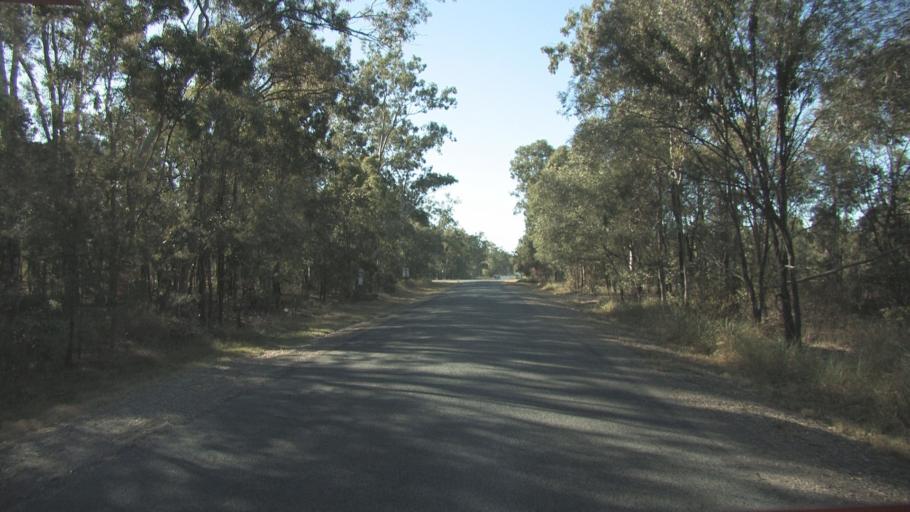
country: AU
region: Queensland
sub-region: Logan
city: North Maclean
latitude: -27.7940
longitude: 153.0267
